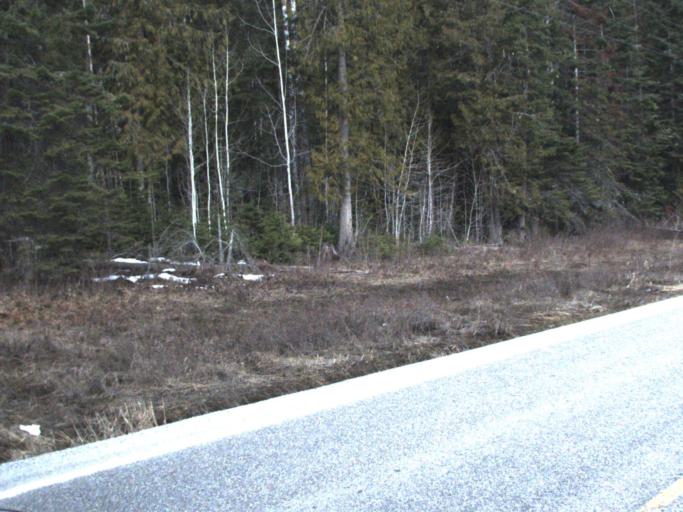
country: US
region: Washington
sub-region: Pend Oreille County
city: Newport
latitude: 48.4535
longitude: -117.3265
